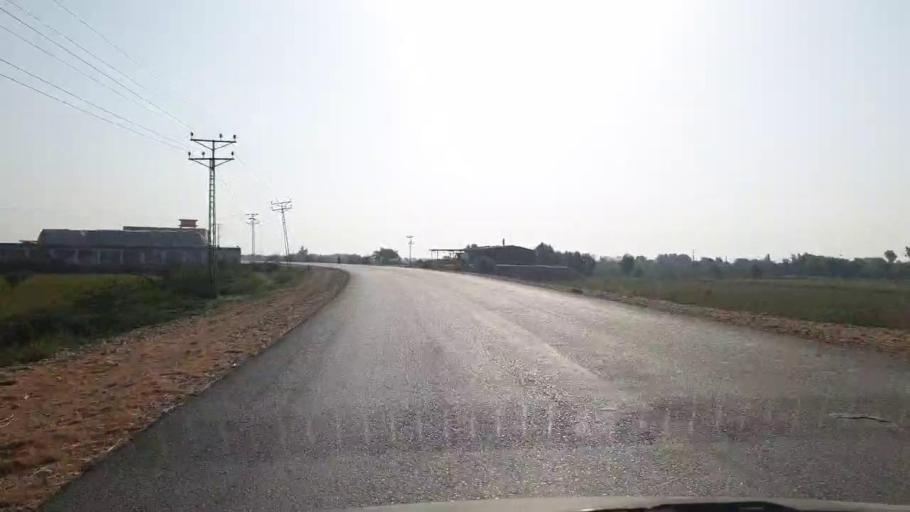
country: PK
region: Sindh
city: Badin
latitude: 24.6607
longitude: 68.8791
